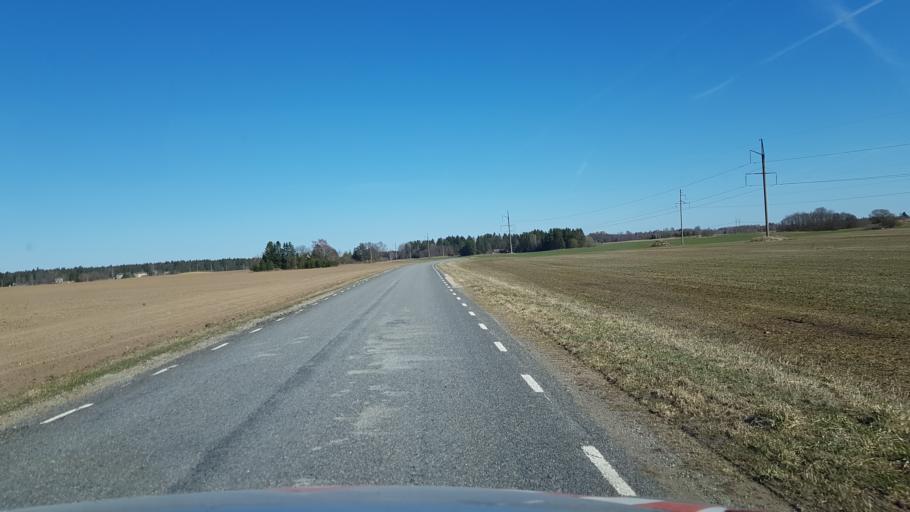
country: EE
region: Laeaene-Virumaa
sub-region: Someru vald
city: Someru
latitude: 59.3271
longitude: 26.5178
